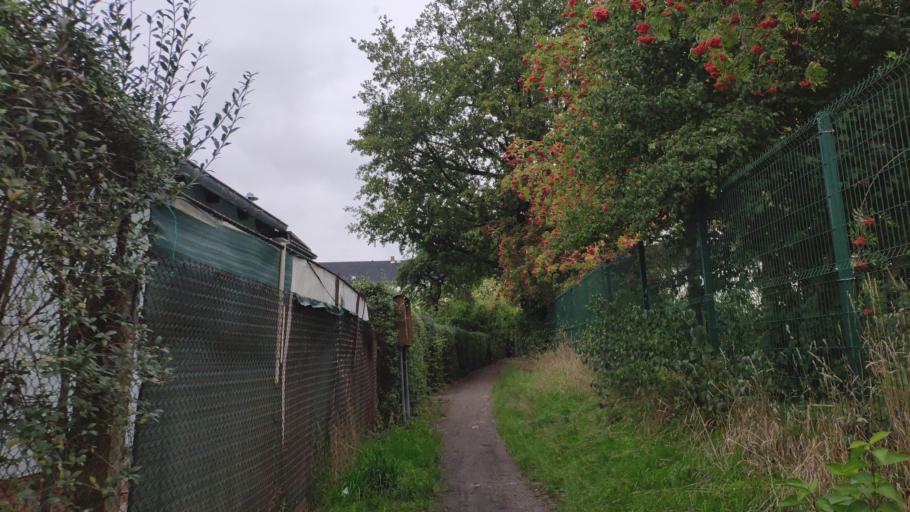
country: DE
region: Saxony
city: Chemnitz
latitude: 50.8277
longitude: 12.9526
